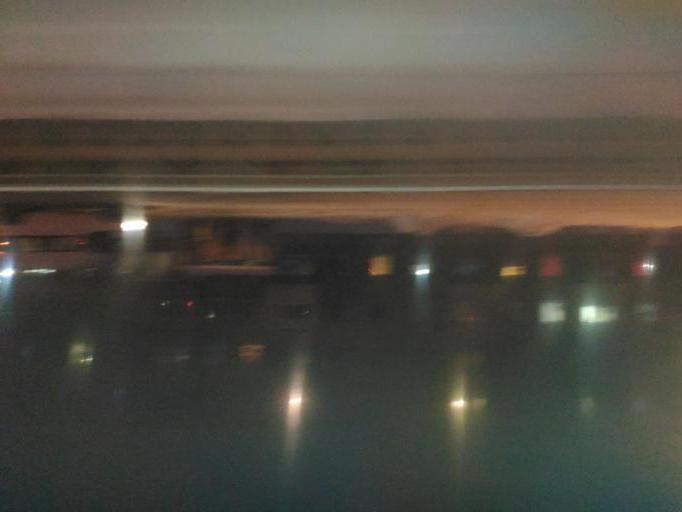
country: RU
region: Ulyanovsk
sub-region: Ulyanovskiy Rayon
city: Ulyanovsk
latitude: 54.3437
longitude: 48.3757
